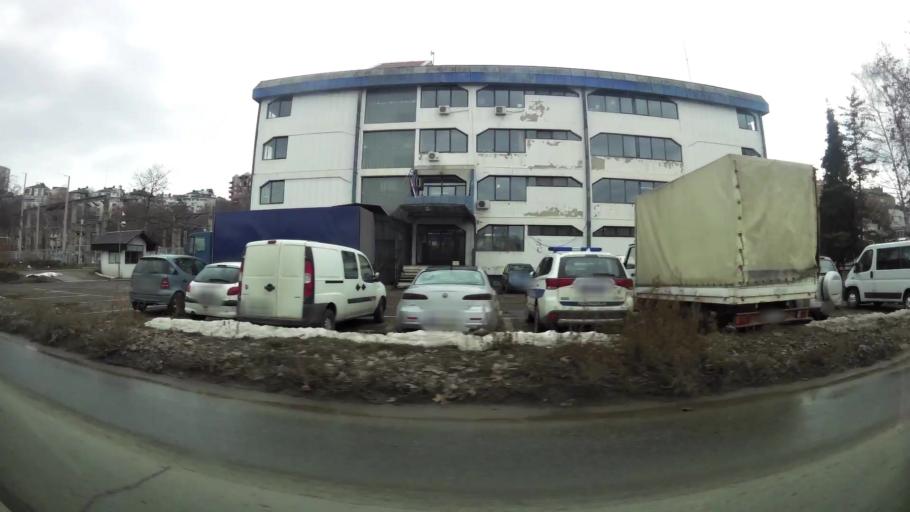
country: RS
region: Central Serbia
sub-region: Belgrade
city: Cukarica
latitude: 44.7639
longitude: 20.4053
